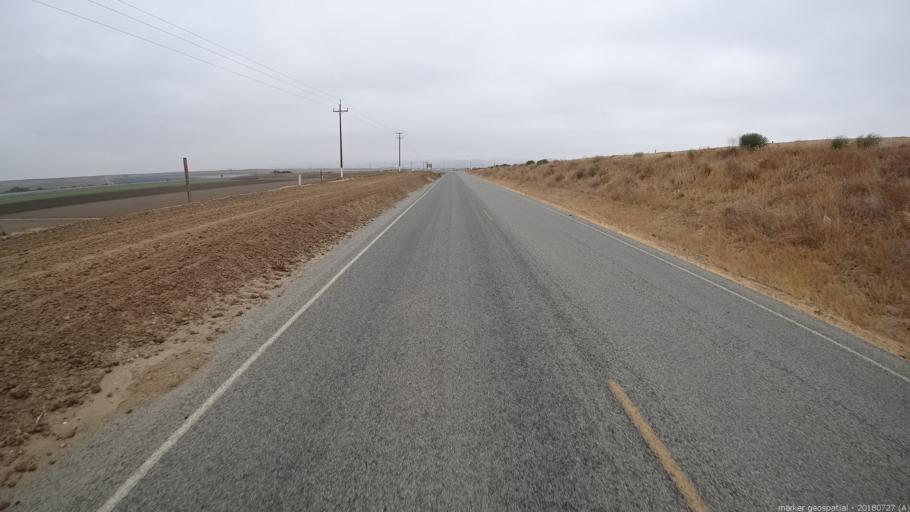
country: US
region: California
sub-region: Monterey County
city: King City
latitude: 36.2410
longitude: -121.1026
